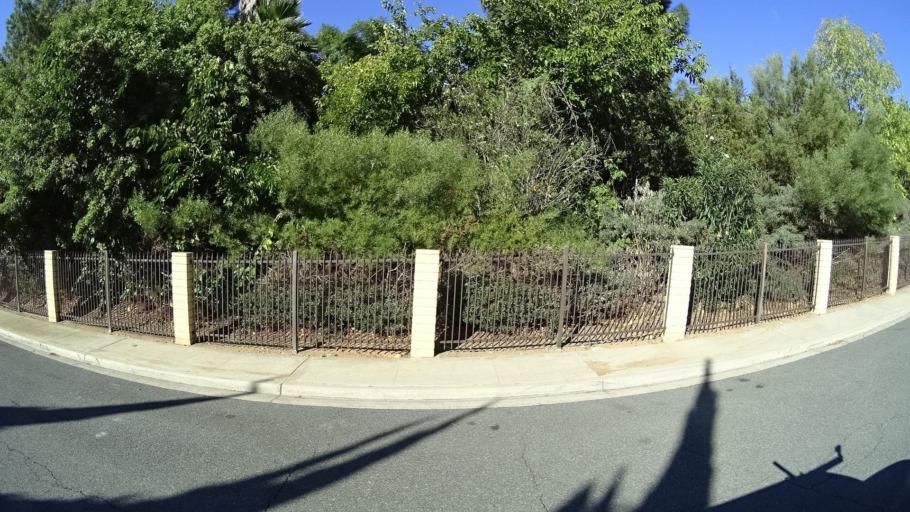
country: US
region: California
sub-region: San Diego County
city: La Presa
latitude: 32.7027
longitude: -116.9989
